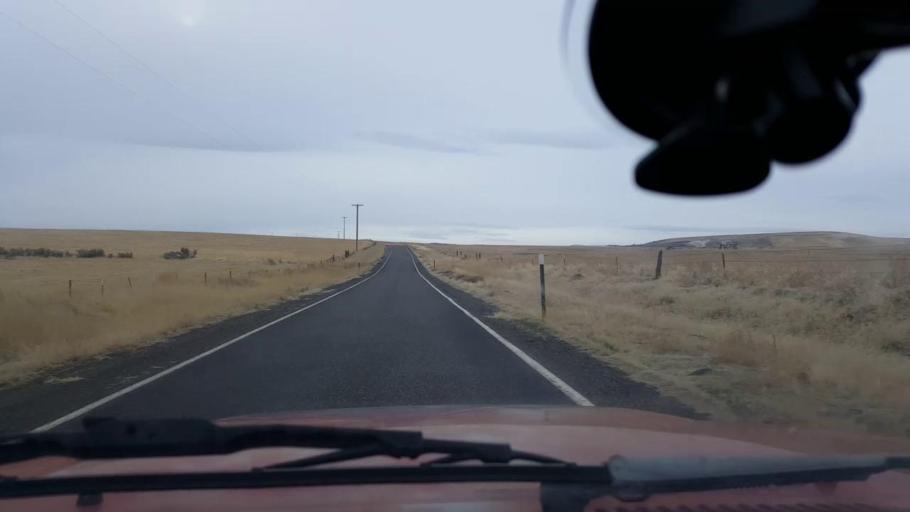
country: US
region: Washington
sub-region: Asotin County
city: Clarkston Heights-Vineland
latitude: 46.3309
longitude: -117.3198
